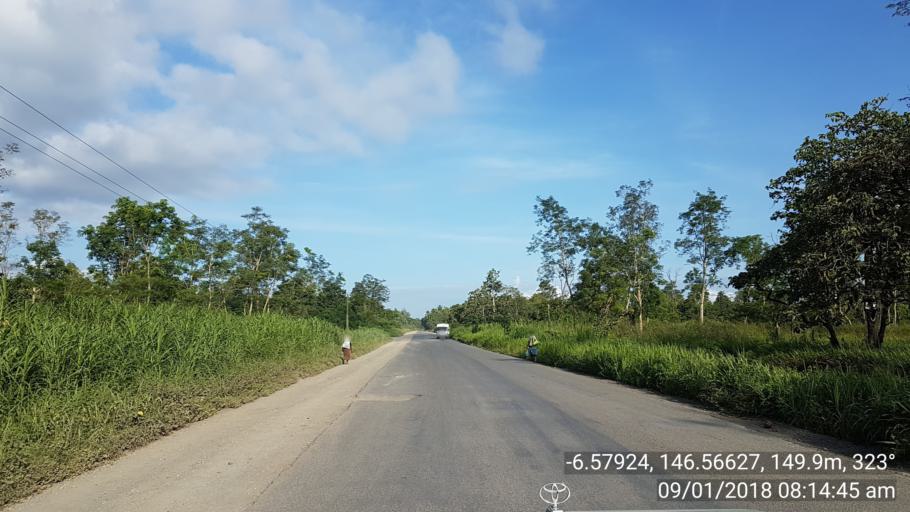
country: PG
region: Morobe
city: Lae
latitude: -6.5793
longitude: 146.5663
